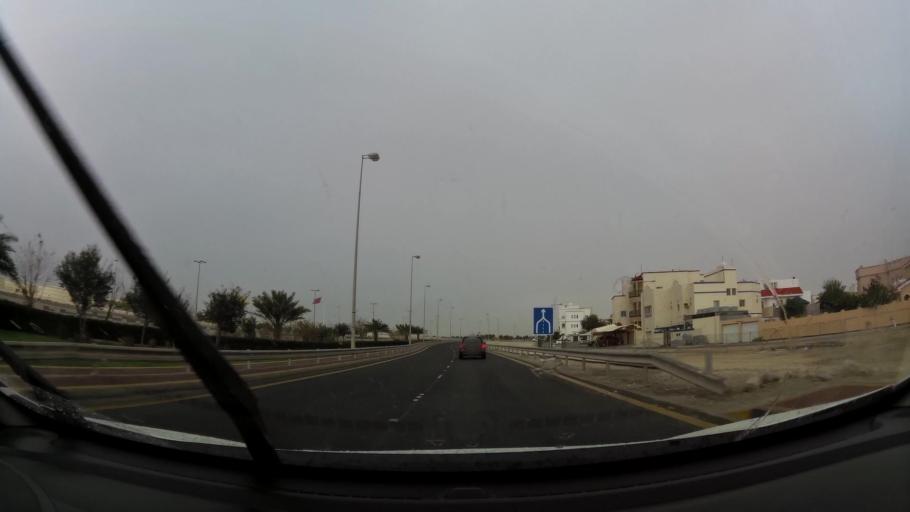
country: BH
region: Central Governorate
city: Madinat Hamad
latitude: 26.1198
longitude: 50.5079
